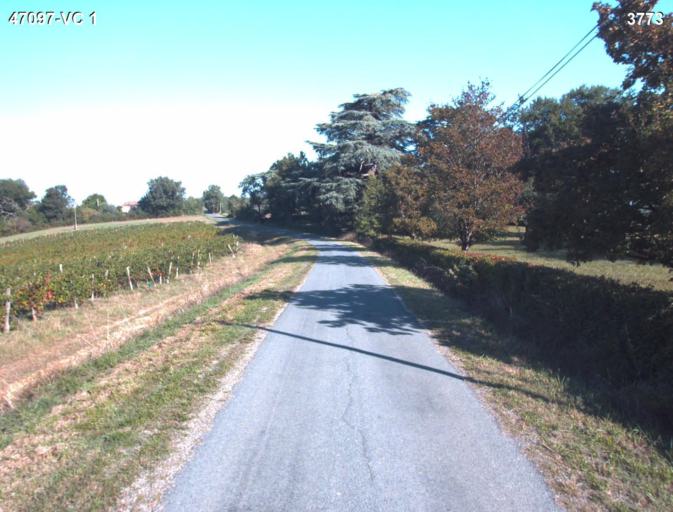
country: FR
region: Aquitaine
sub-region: Departement du Lot-et-Garonne
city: Vianne
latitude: 44.1937
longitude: 0.3646
